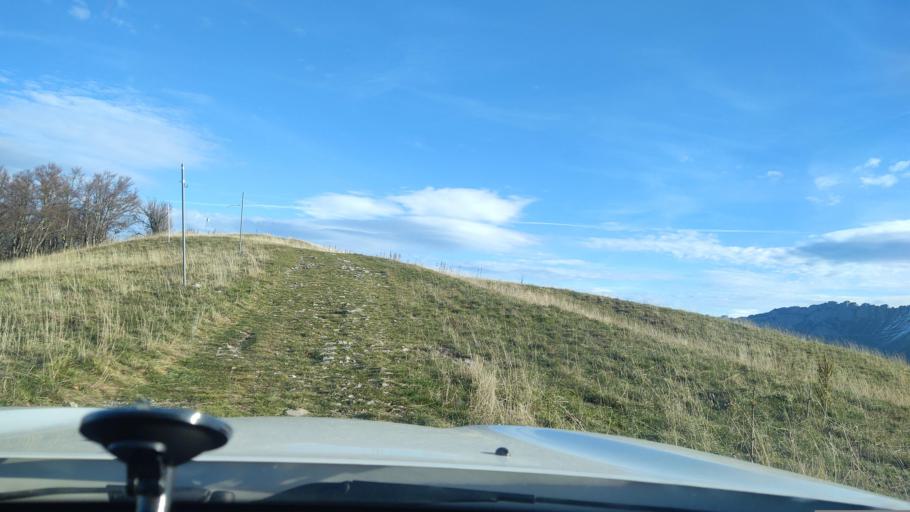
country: FR
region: Rhone-Alpes
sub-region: Departement de la Savoie
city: Cruet
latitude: 45.5914
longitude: 6.1111
